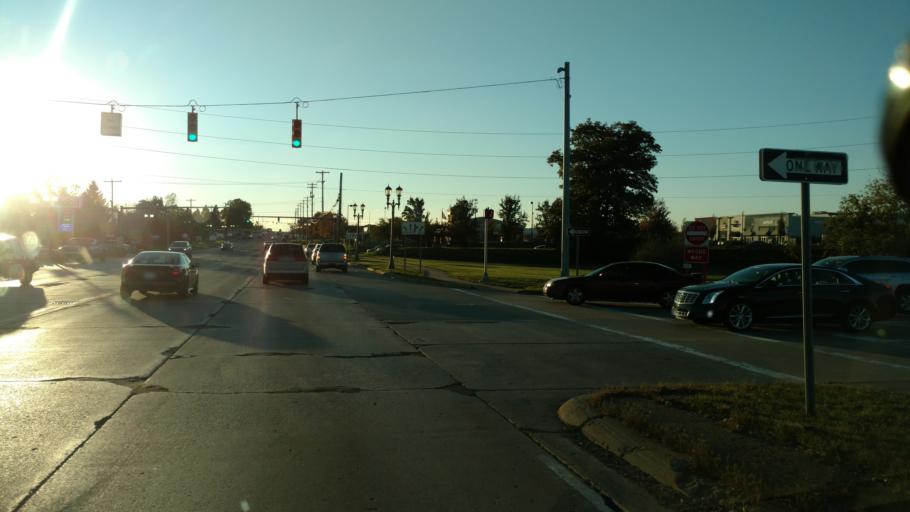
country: US
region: Michigan
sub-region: Ingham County
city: East Lansing
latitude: 42.7608
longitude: -84.5118
